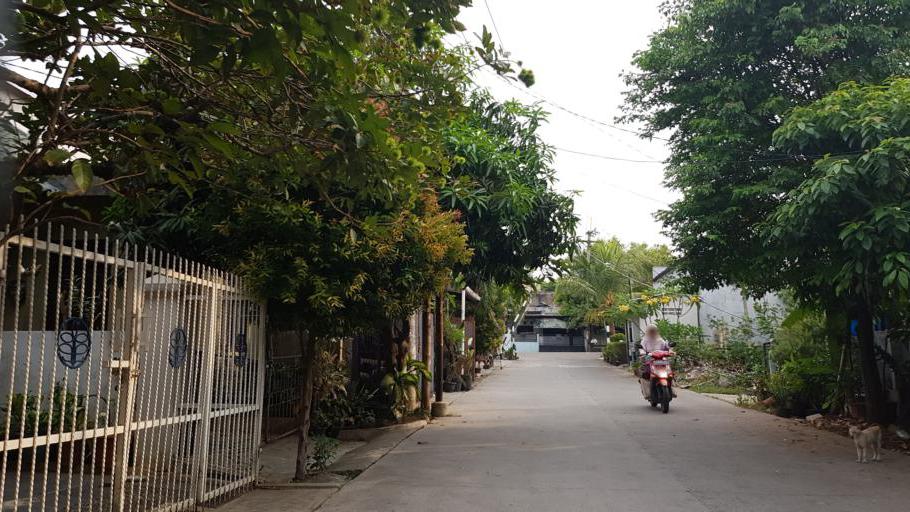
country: ID
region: West Java
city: Depok
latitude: -6.3721
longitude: 106.7951
